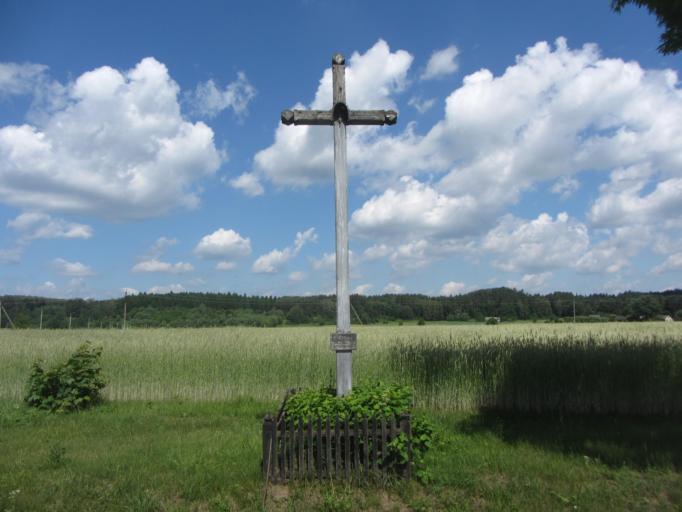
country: LT
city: Birstonas
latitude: 54.5516
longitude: 24.0208
